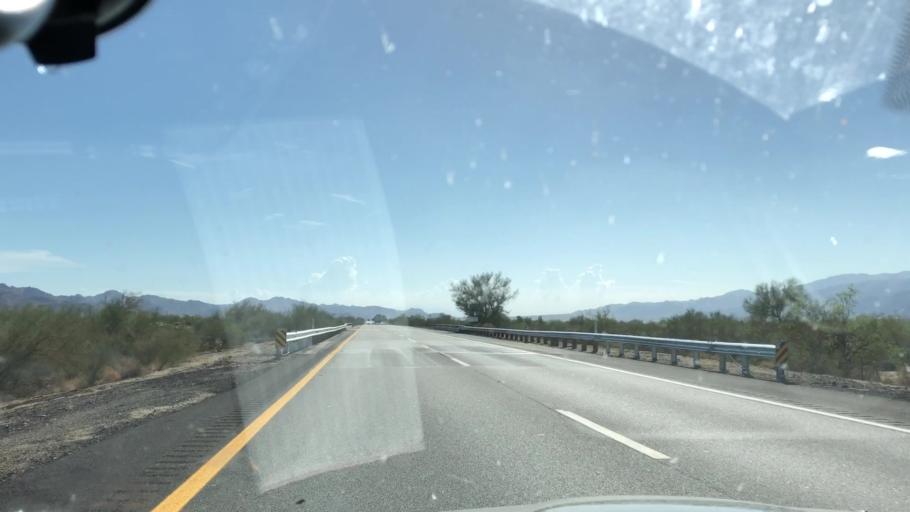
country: US
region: California
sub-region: Imperial County
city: Niland
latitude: 33.6836
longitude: -115.5379
